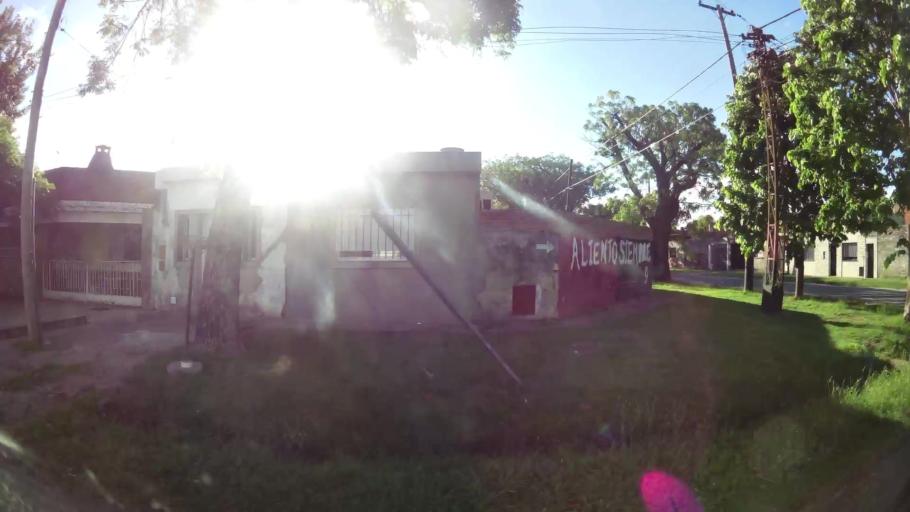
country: AR
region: Santa Fe
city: Gobernador Galvez
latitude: -32.9895
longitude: -60.6691
